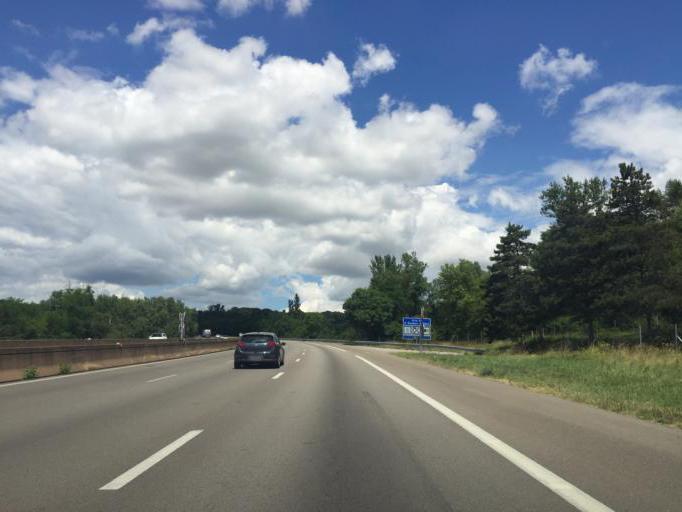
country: FR
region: Rhone-Alpes
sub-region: Departement de la Drome
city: Saint-Uze
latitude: 45.2017
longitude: 4.8774
